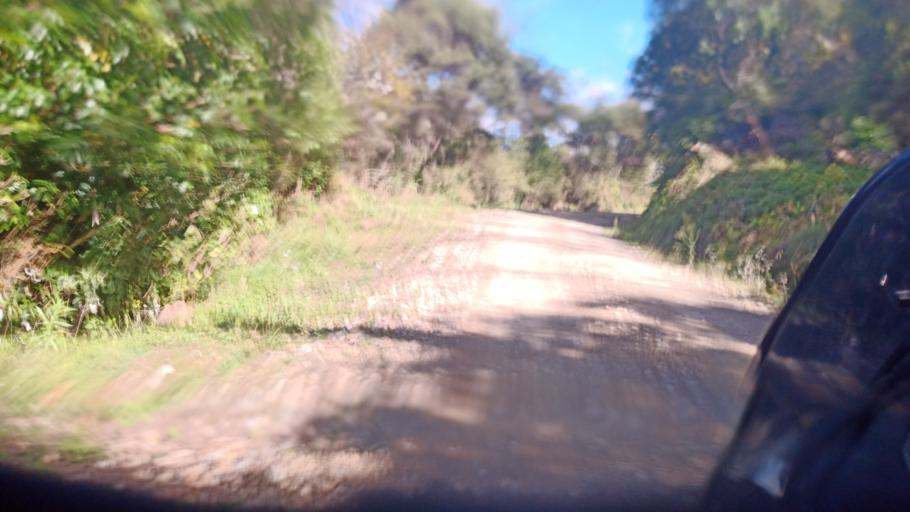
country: NZ
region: Gisborne
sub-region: Gisborne District
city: Gisborne
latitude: -38.3902
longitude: 177.6595
